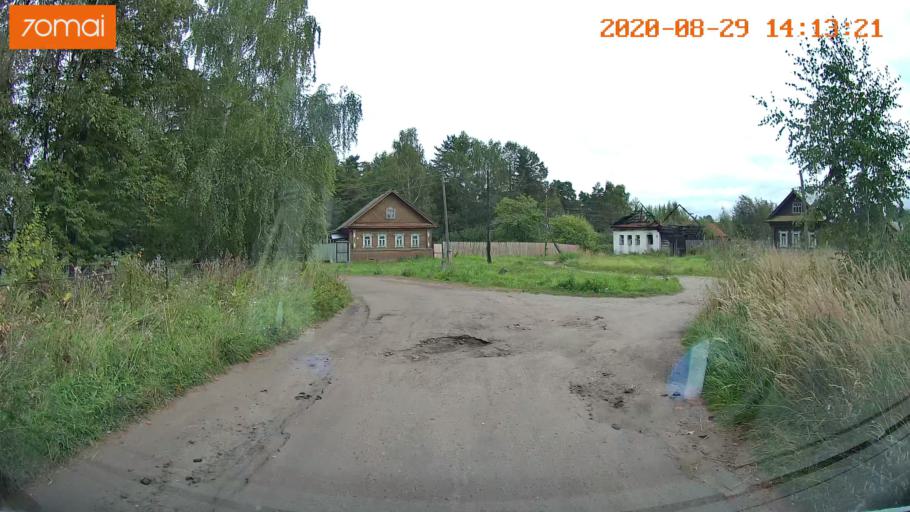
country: RU
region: Ivanovo
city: Yur'yevets
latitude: 57.3146
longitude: 43.1011
